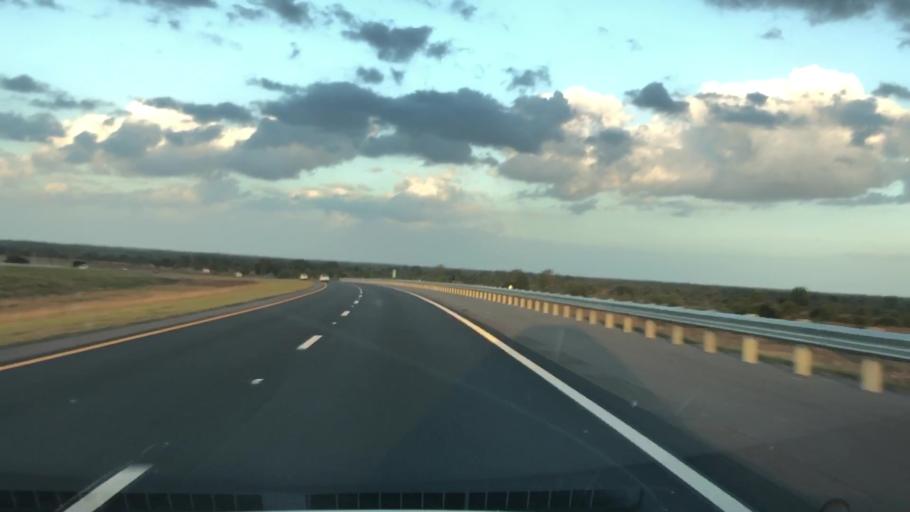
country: US
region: Florida
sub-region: Lake County
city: Mount Plymouth
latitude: 28.7778
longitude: -81.5258
